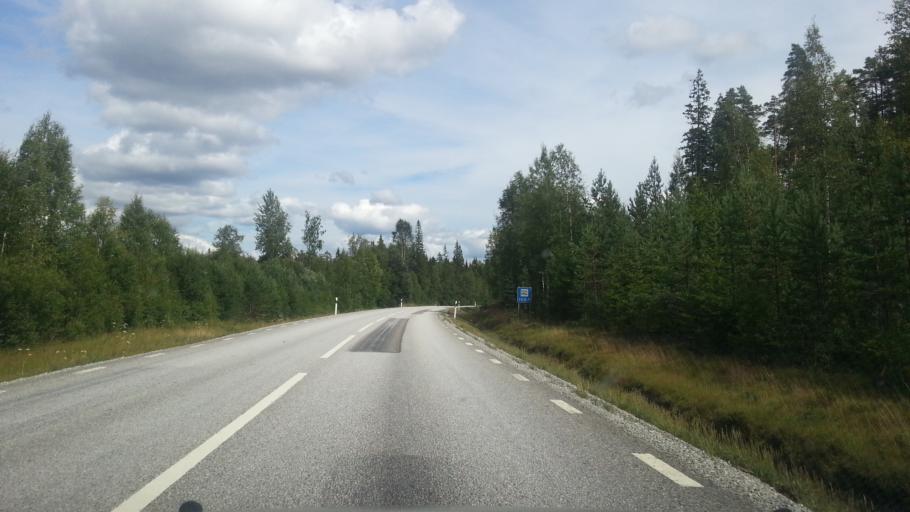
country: SE
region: Vaestmanland
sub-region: Skinnskattebergs Kommun
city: Skinnskatteberg
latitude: 59.7704
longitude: 15.5216
